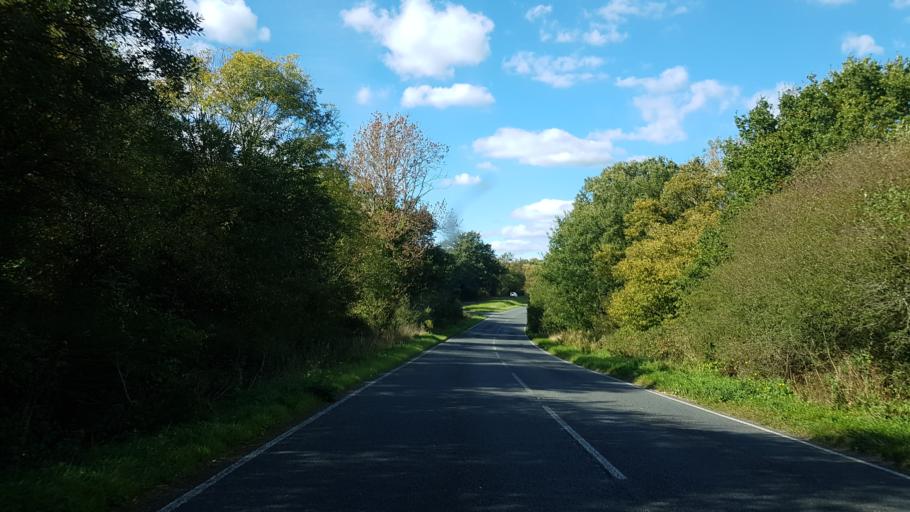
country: GB
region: England
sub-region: West Sussex
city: Petworth
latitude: 51.0298
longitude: -0.6302
